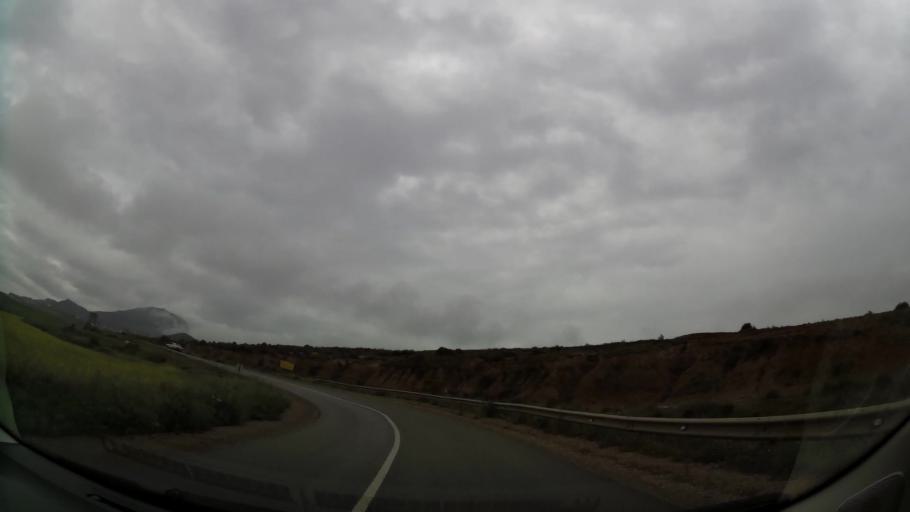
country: MA
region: Oriental
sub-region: Nador
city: Nador
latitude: 35.1502
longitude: -3.0411
